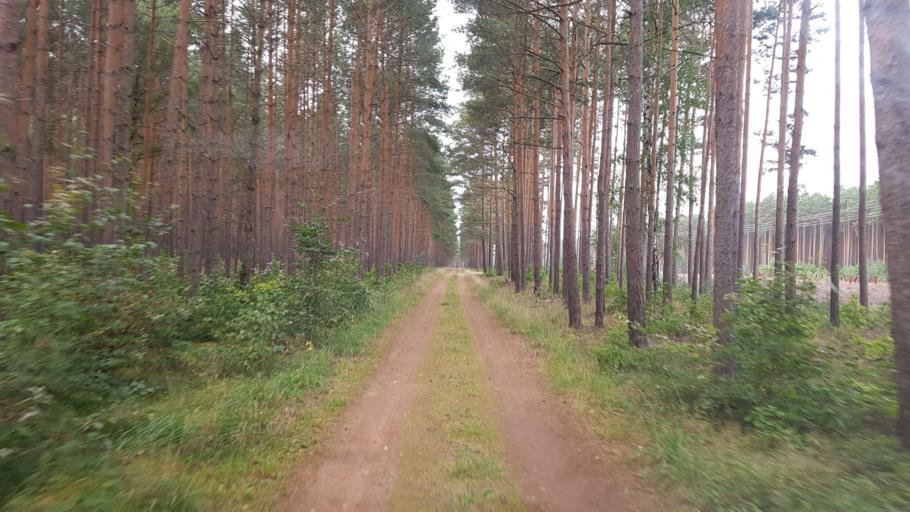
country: DE
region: Brandenburg
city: Hohenbucko
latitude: 51.7773
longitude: 13.5633
